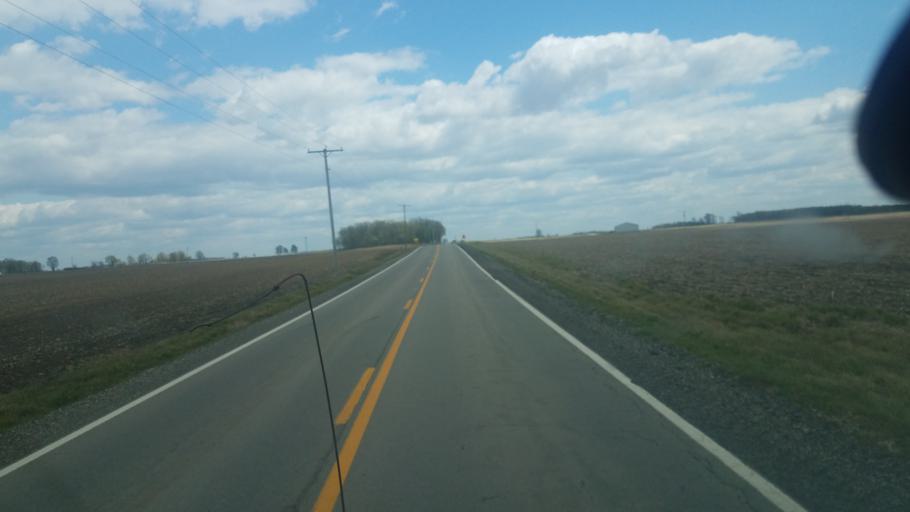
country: US
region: Ohio
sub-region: Crawford County
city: Bucyrus
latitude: 40.7171
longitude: -83.0063
